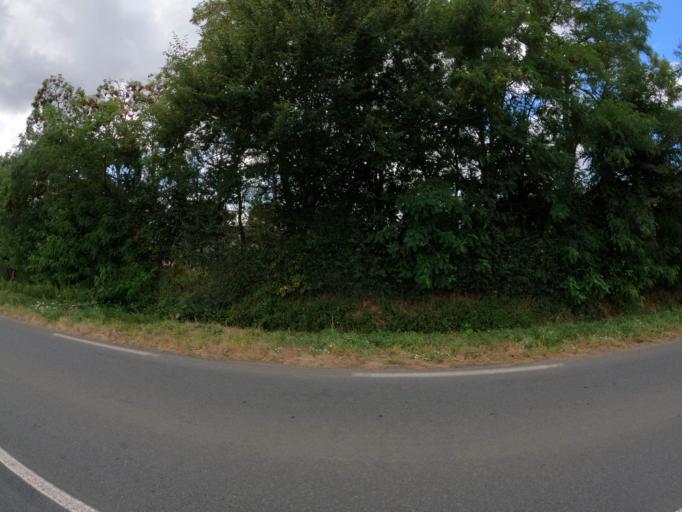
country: FR
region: Pays de la Loire
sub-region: Departement de la Sarthe
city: Solesmes
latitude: 47.8584
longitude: -0.3199
